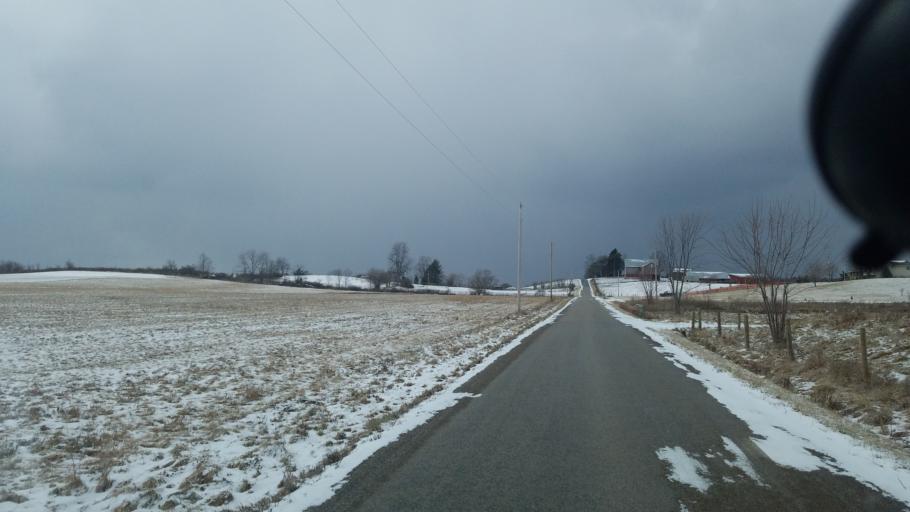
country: US
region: Ohio
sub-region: Morrow County
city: Mount Gilead
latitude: 40.5436
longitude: -82.7219
